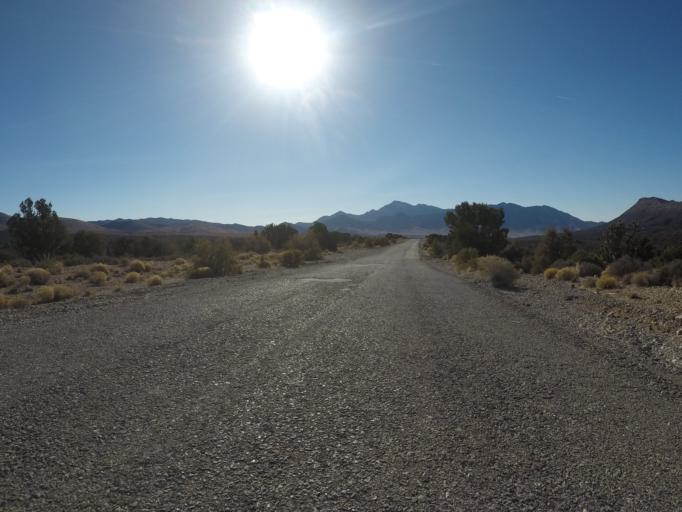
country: US
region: Nevada
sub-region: Clark County
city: Summerlin South
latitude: 36.0749
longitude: -115.5640
